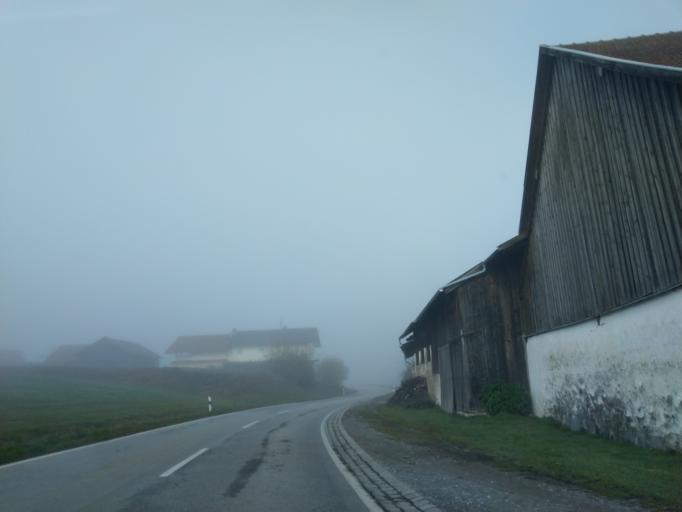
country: DE
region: Bavaria
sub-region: Lower Bavaria
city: Aussernzell
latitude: 48.7412
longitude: 13.1963
